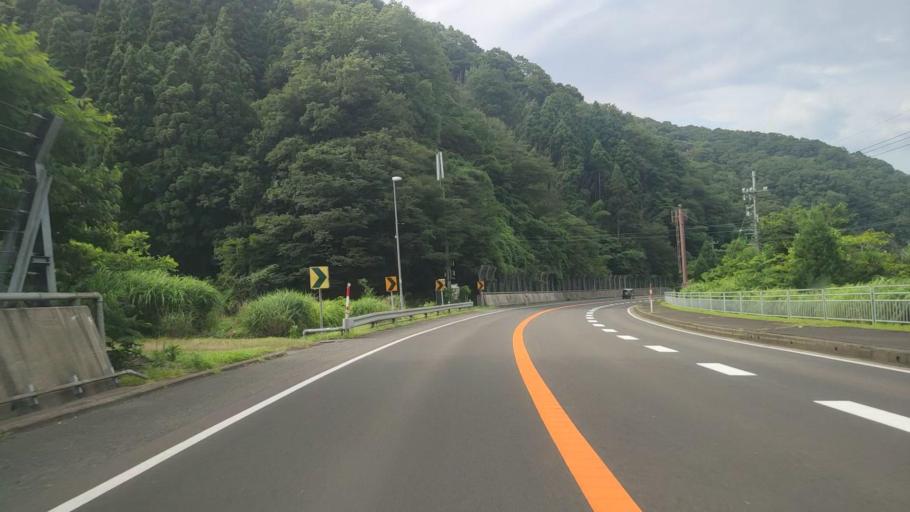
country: JP
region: Fukui
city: Takefu
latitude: 35.8086
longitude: 136.0950
